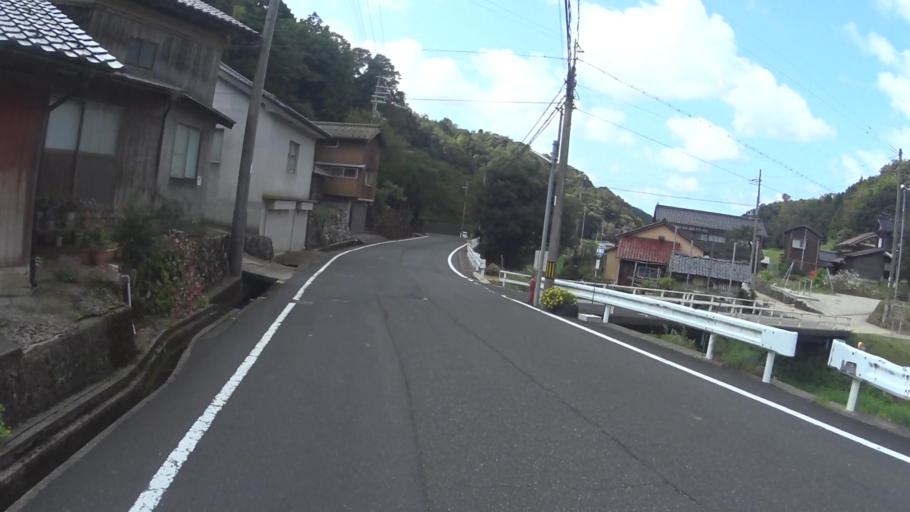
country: JP
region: Kyoto
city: Miyazu
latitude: 35.7434
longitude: 135.1823
